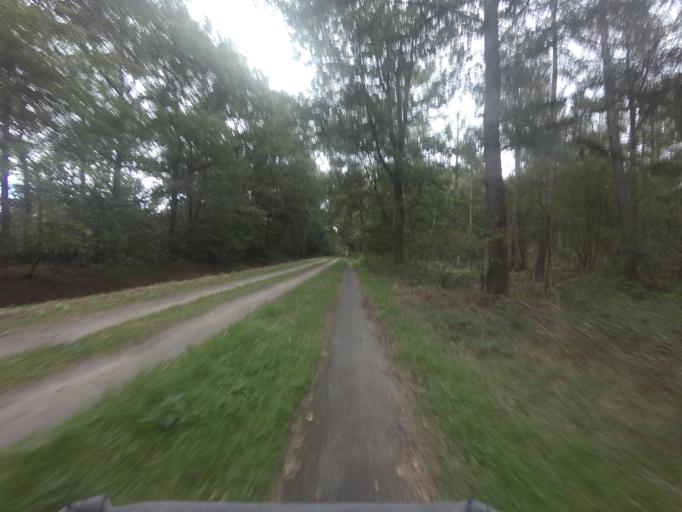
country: NL
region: Friesland
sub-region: Gemeente Weststellingwerf
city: Noordwolde
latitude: 52.9092
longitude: 6.2279
